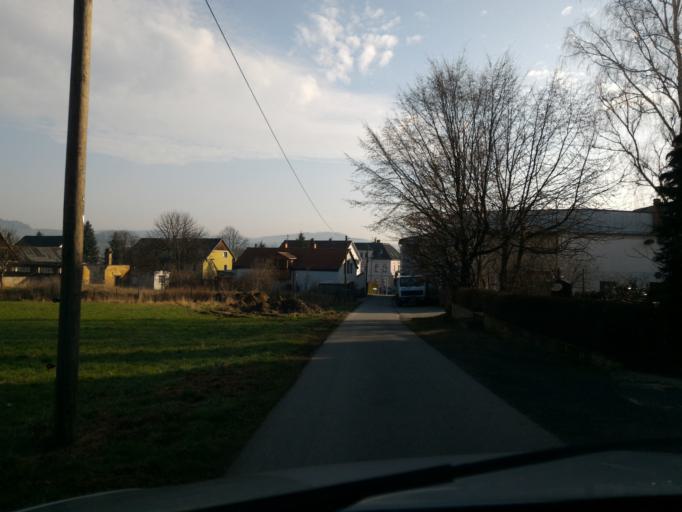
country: DE
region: Saxony
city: Grossschonau
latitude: 50.8976
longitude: 14.6537
